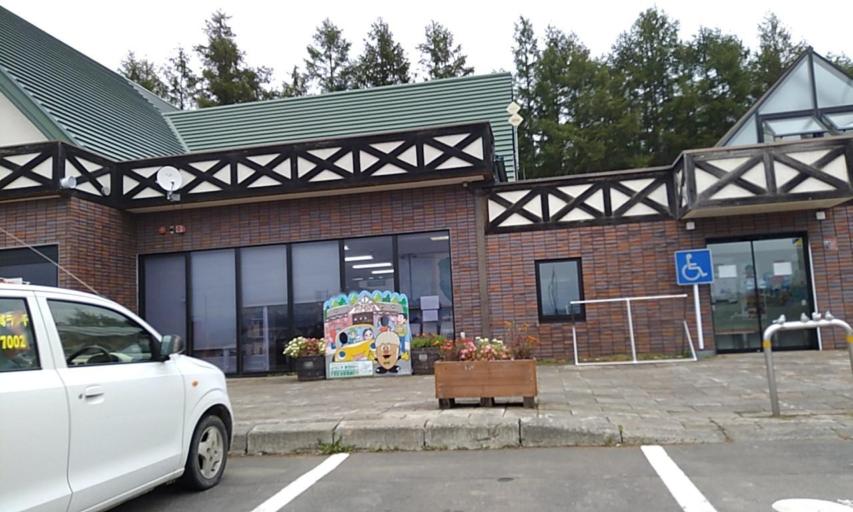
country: JP
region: Hokkaido
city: Obihiro
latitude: 42.6331
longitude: 143.2719
